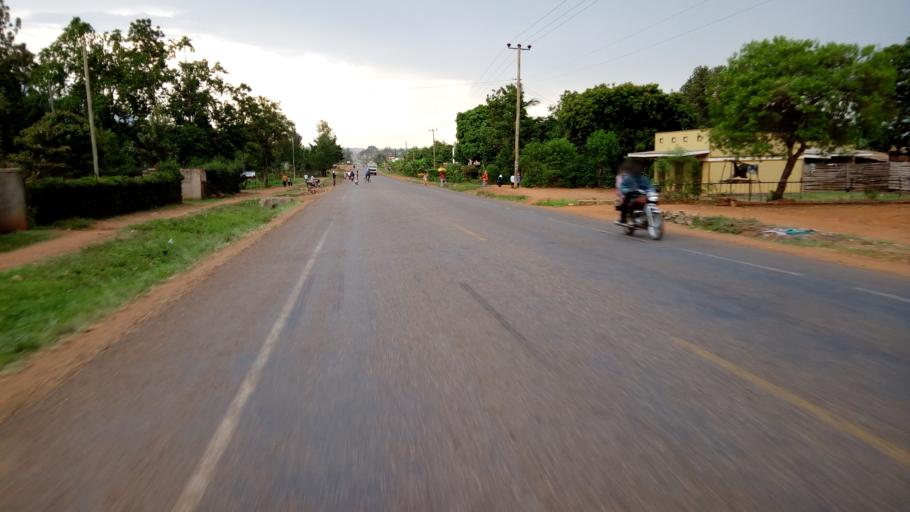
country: UG
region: Eastern Region
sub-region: Mbale District
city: Mbale
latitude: 1.1193
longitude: 34.1698
